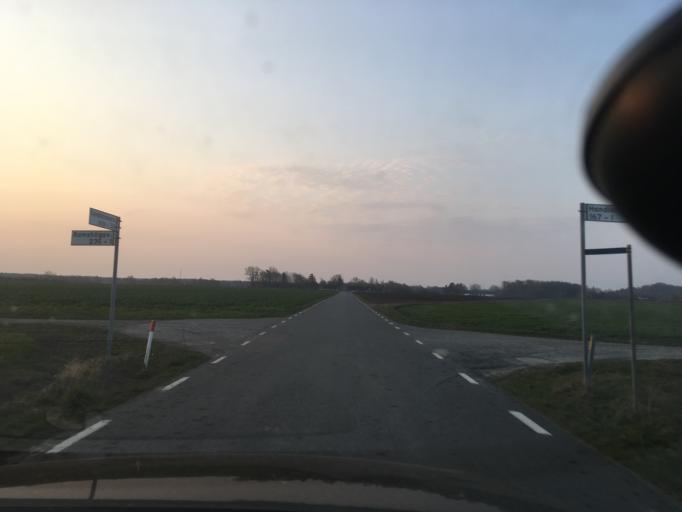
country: SE
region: Skane
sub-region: Ystads Kommun
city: Kopingebro
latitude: 55.4059
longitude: 14.1582
